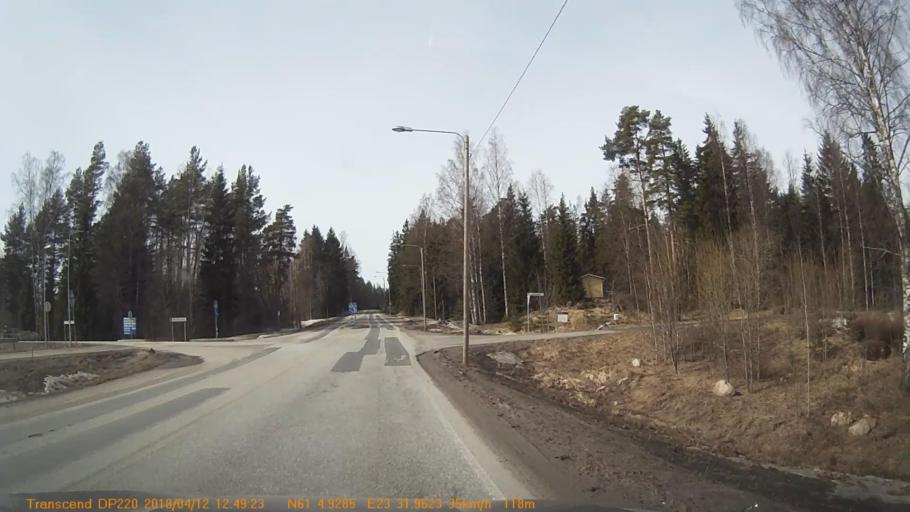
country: FI
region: Pirkanmaa
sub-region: Etelae-Pirkanmaa
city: Urjala
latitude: 61.0822
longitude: 23.5325
